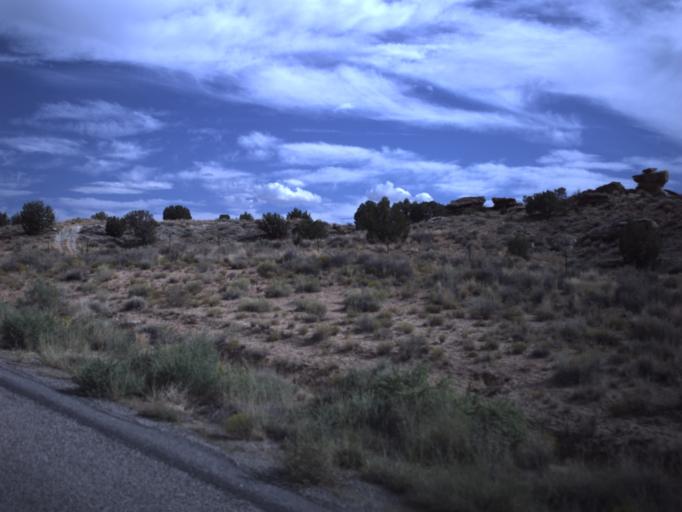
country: US
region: Colorado
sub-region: Montezuma County
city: Towaoc
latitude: 37.1917
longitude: -109.1373
